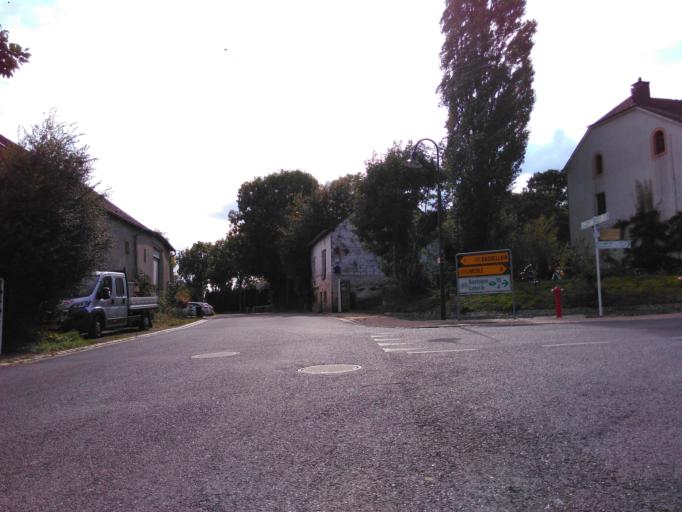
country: LU
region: Diekirch
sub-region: Canton de Clervaux
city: Troisvierges
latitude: 50.1552
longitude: 5.9761
